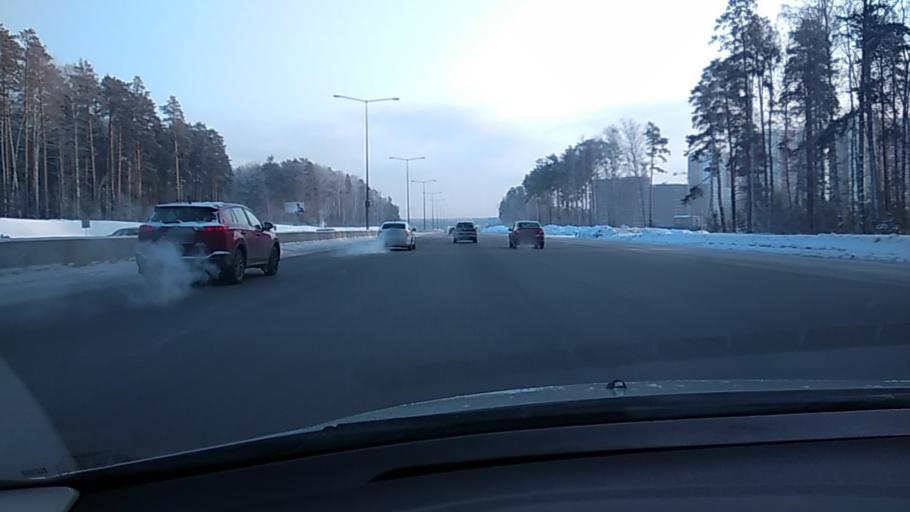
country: RU
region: Sverdlovsk
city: Istok
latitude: 56.7832
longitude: 60.6955
